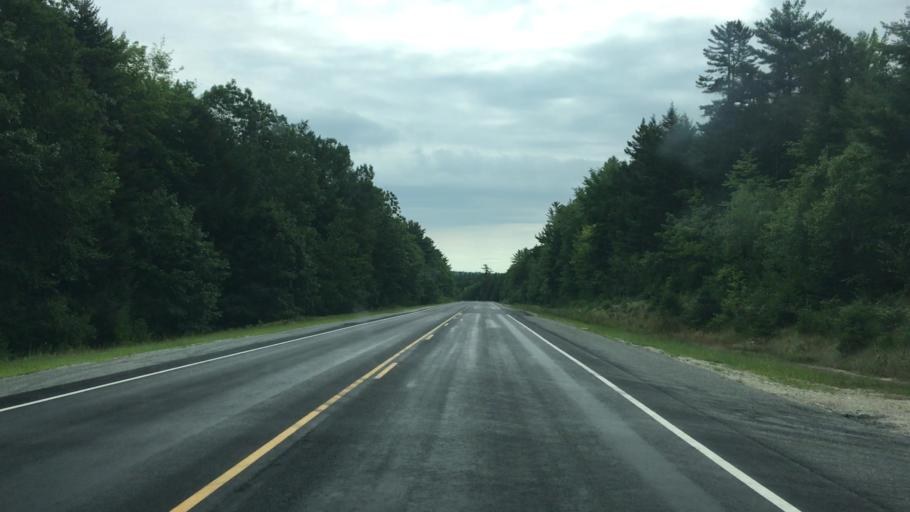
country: US
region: Maine
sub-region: Washington County
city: Addison
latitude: 44.9100
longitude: -67.8491
